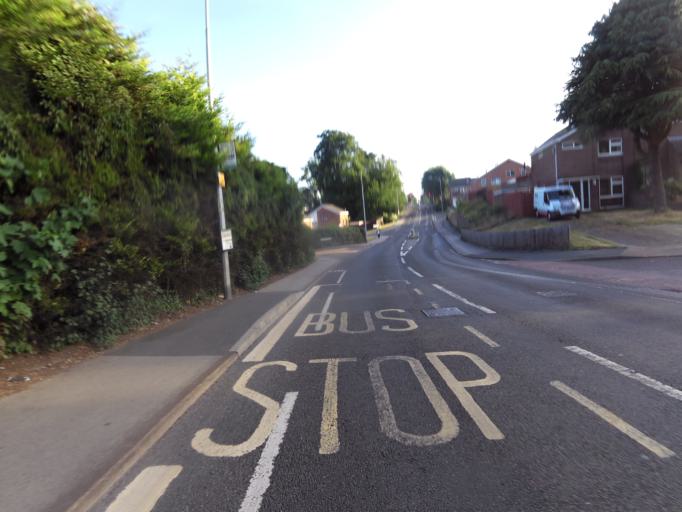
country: GB
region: England
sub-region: Suffolk
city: Ipswich
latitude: 52.0403
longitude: 1.1383
